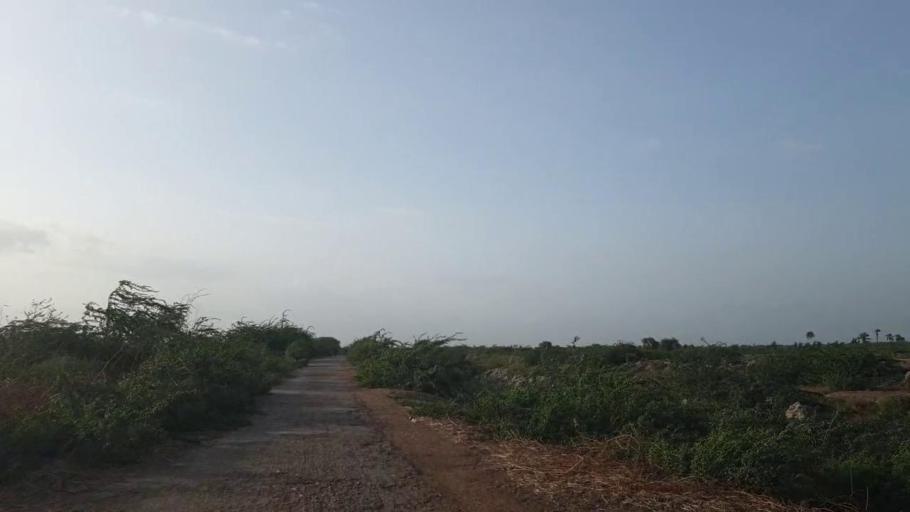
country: PK
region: Sindh
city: Kadhan
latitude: 24.6310
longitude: 69.1588
